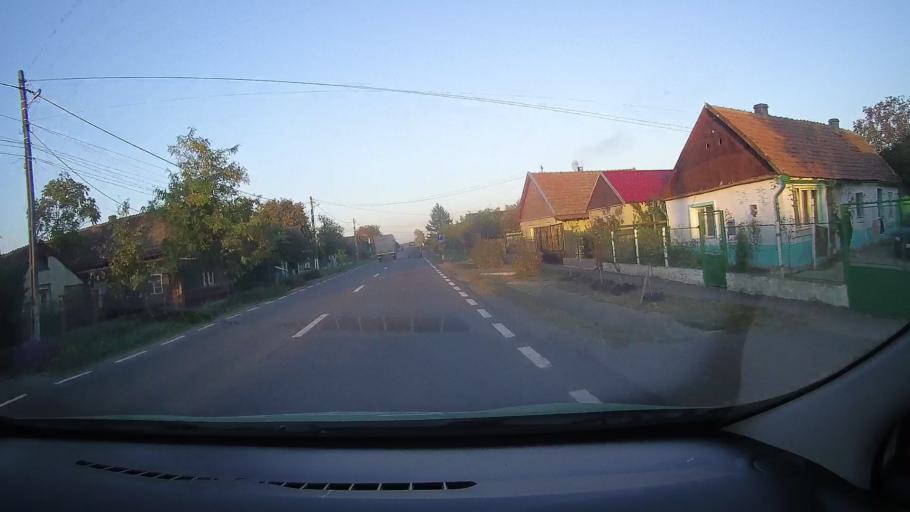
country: RO
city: Dioszeg
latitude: 47.2851
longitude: 21.9919
